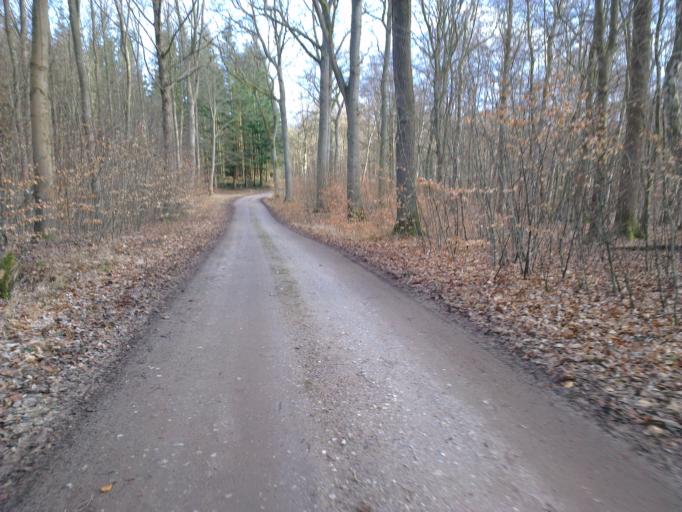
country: DK
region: Capital Region
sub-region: Frederikssund Kommune
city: Jaegerspris
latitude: 55.8946
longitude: 12.0072
